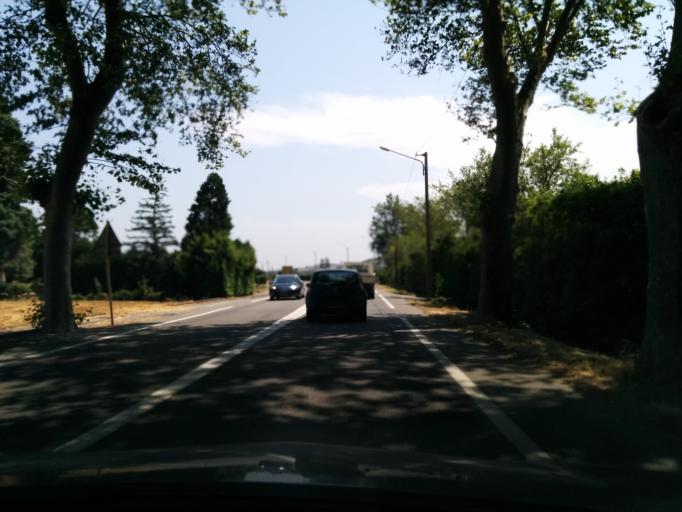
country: FR
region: Midi-Pyrenees
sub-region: Departement de la Haute-Garonne
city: Villefranche-de-Lauragais
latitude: 43.3886
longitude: 1.7281
